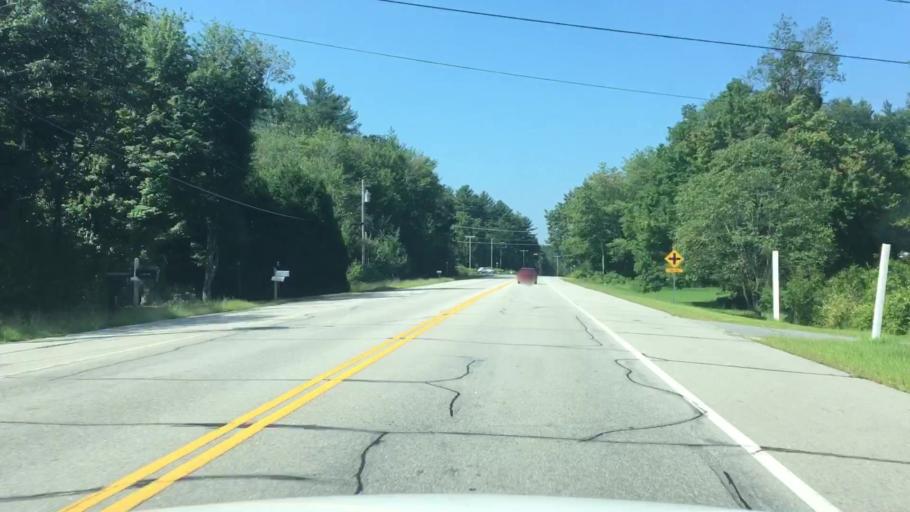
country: US
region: New Hampshire
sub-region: Rockingham County
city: Danville
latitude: 42.9095
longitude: -71.0841
